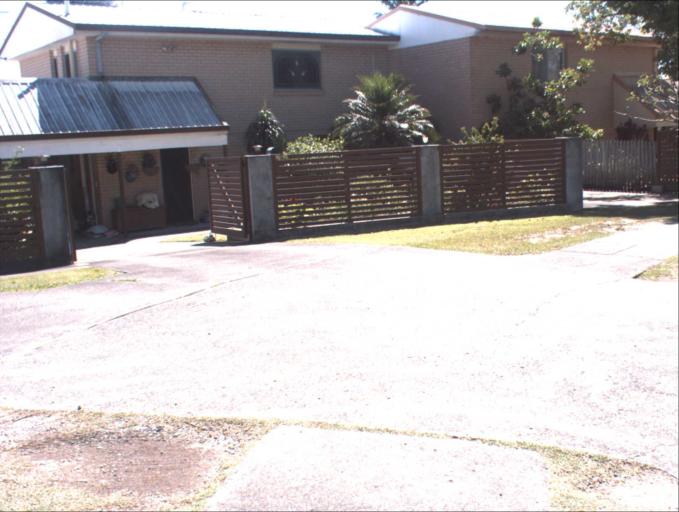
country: AU
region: Queensland
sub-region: Logan
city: Woodridge
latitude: -27.6246
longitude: 153.1113
